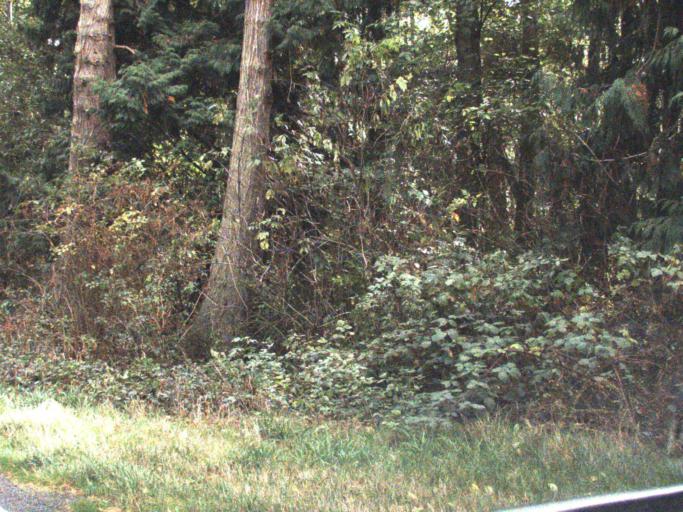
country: US
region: Washington
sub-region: Island County
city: Coupeville
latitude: 48.1746
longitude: -122.6148
